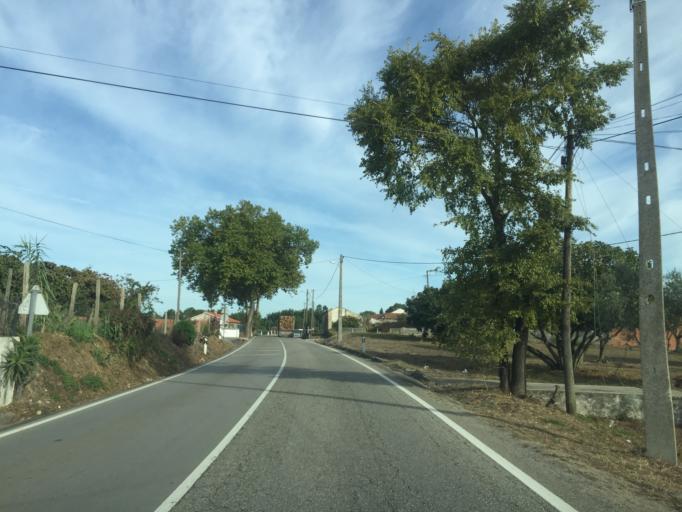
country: PT
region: Leiria
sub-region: Pombal
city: Lourical
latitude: 39.9996
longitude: -8.8044
